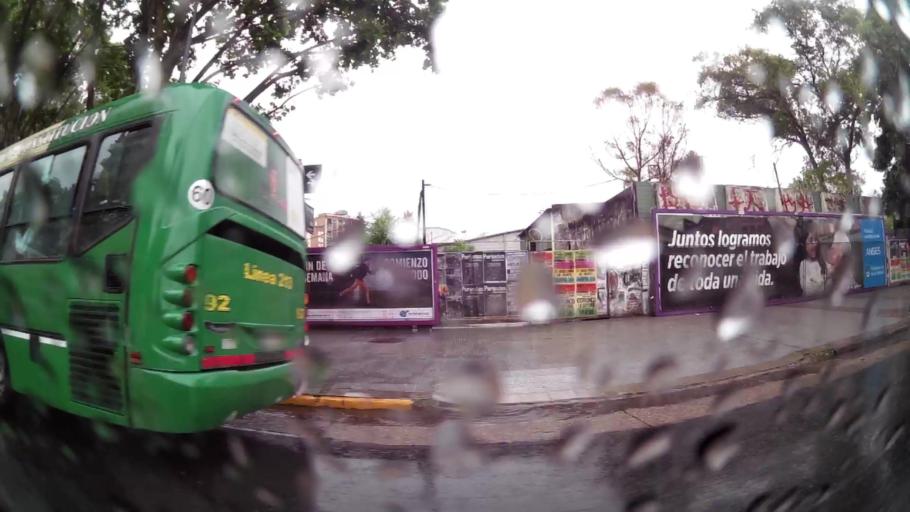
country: AR
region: Buenos Aires F.D.
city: Buenos Aires
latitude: -34.6278
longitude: -58.3674
